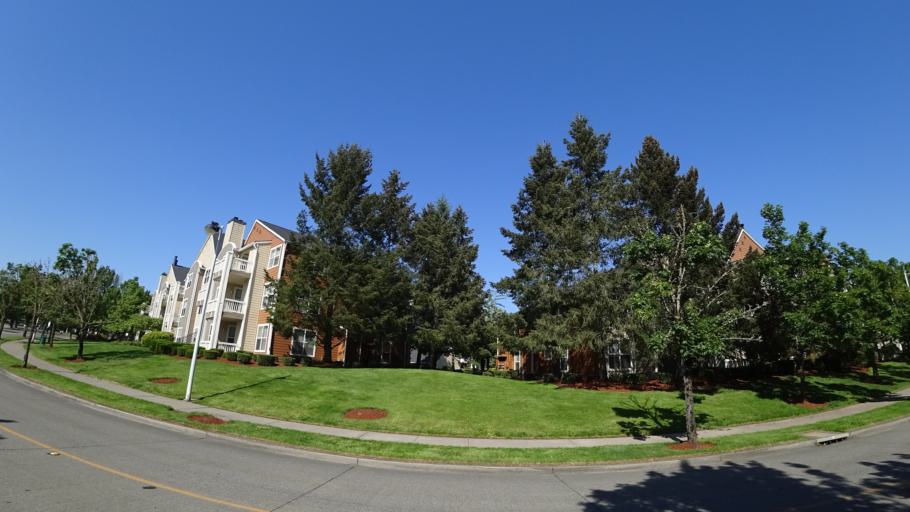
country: US
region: Oregon
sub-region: Washington County
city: Beaverton
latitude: 45.4940
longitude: -122.8340
